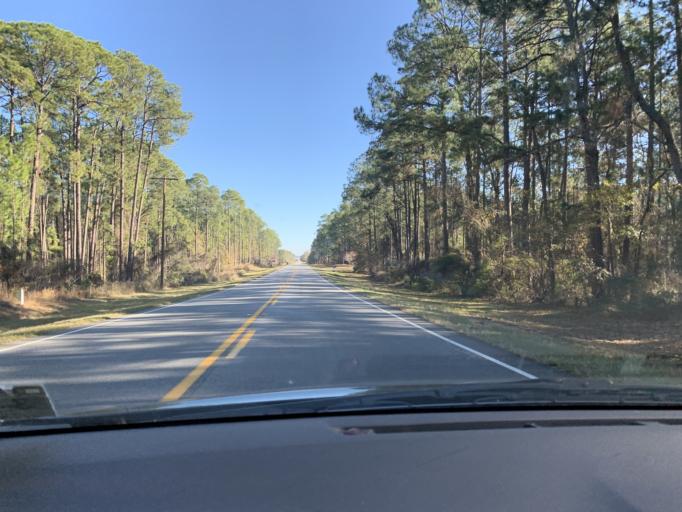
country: US
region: Georgia
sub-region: Ben Hill County
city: Fitzgerald
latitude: 31.7312
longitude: -83.1728
